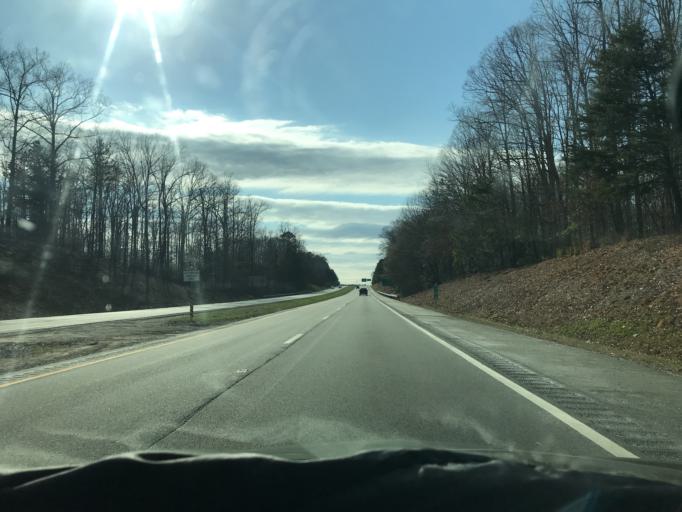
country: US
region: Virginia
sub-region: Chesterfield County
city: Brandermill
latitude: 37.4627
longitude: -77.6233
